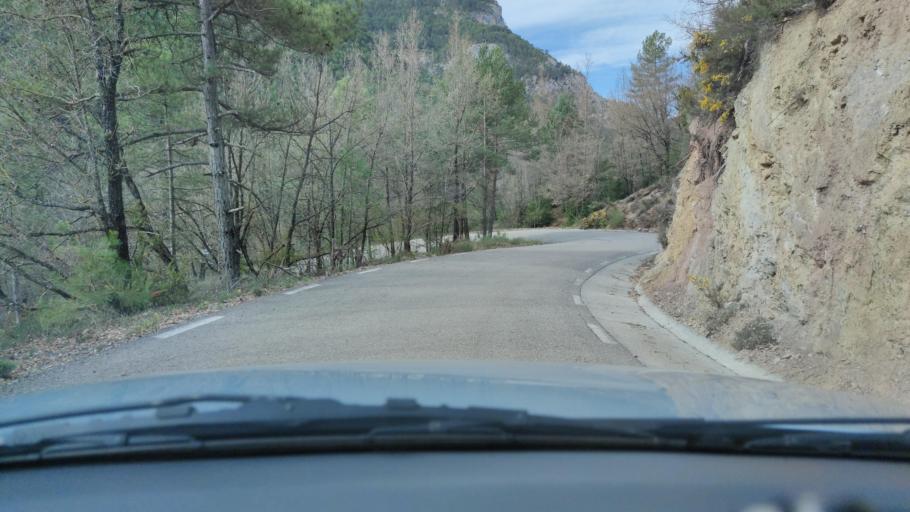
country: ES
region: Catalonia
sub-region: Provincia de Lleida
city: la Seu d'Urgell
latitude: 42.2399
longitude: 1.4329
